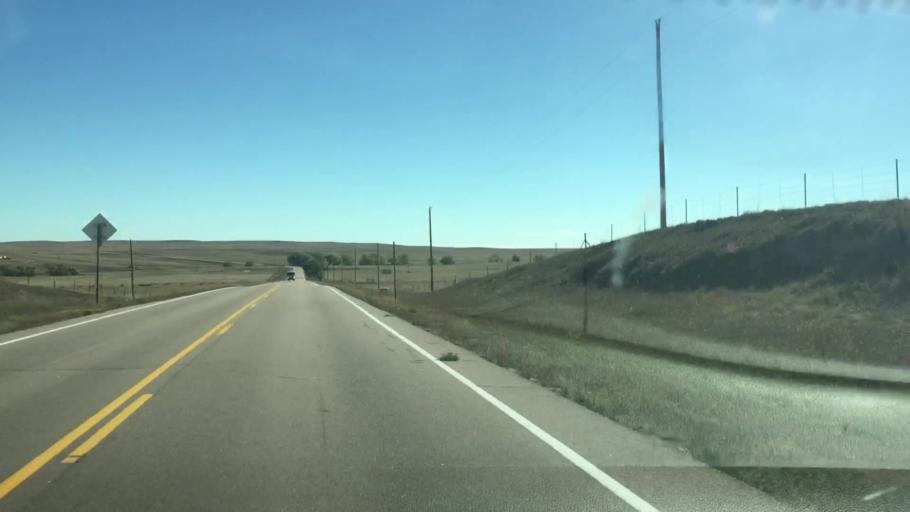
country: US
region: Colorado
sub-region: Lincoln County
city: Limon
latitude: 39.2735
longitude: -104.0212
